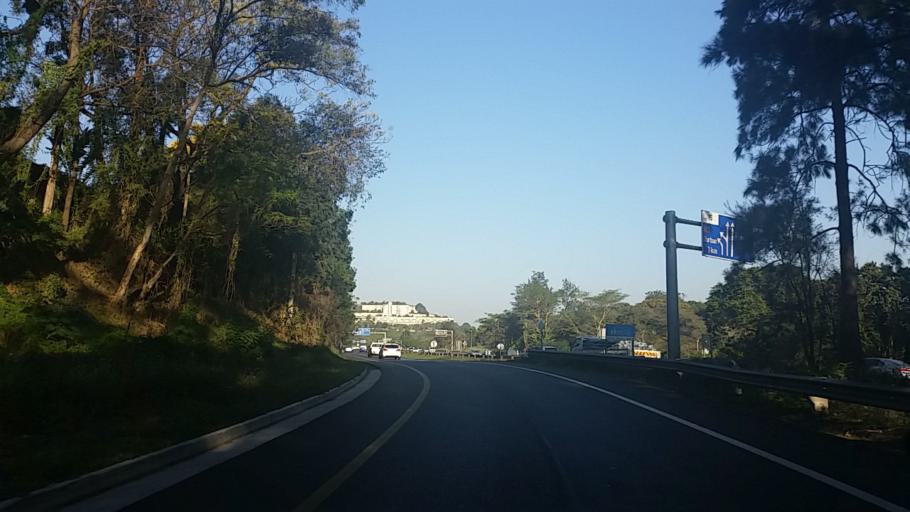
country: ZA
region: KwaZulu-Natal
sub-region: eThekwini Metropolitan Municipality
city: Berea
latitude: -29.8271
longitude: 30.8789
